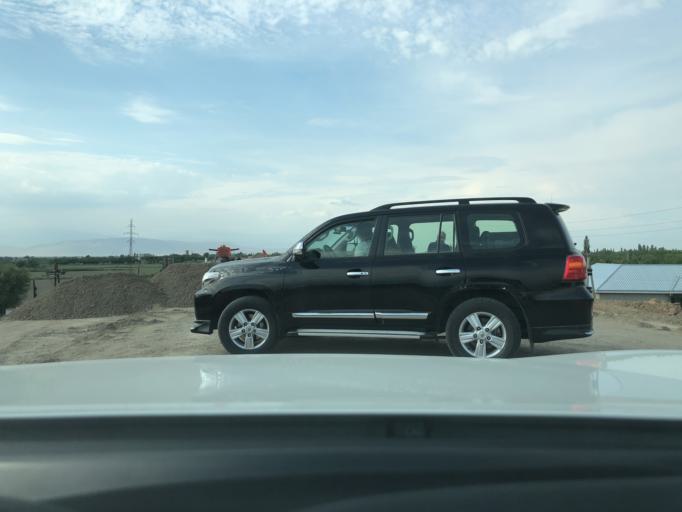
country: TJ
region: Viloyati Sughd
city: Konibodom
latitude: 40.3127
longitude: 70.4255
